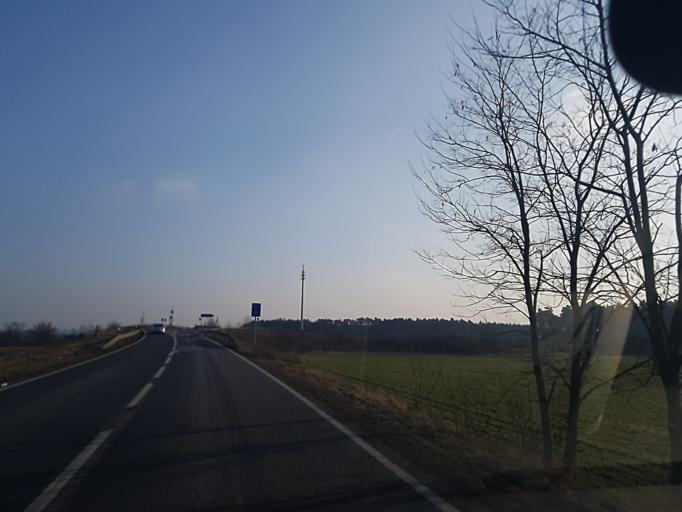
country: DE
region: Brandenburg
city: Wenzlow
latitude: 52.2938
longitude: 12.4592
